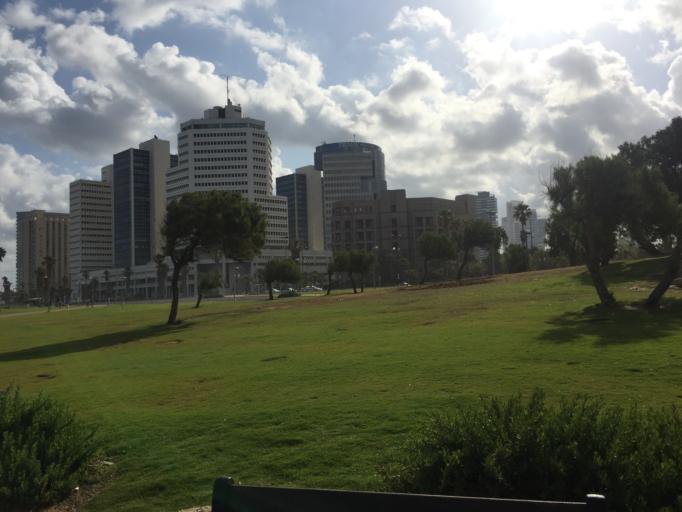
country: IL
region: Tel Aviv
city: Yafo
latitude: 32.0617
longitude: 34.7599
